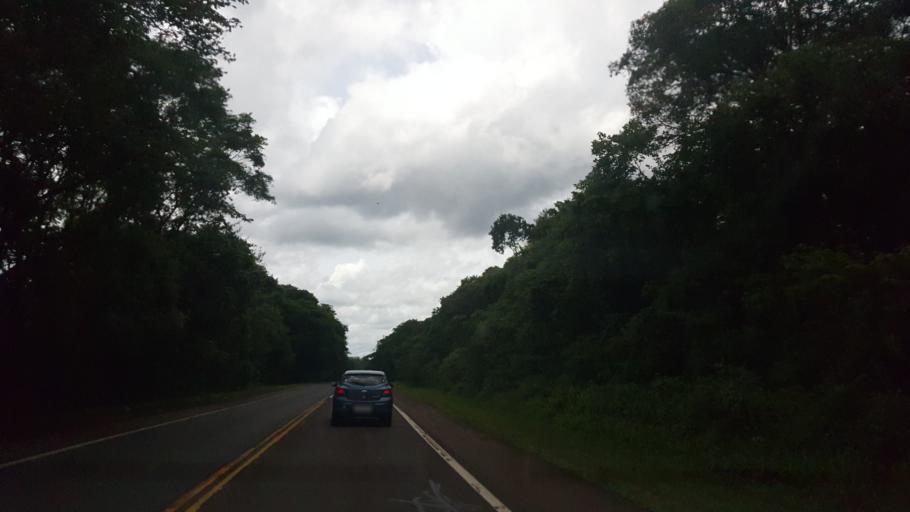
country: AR
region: Misiones
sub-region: Departamento de Iguazu
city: Puerto Iguazu
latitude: -25.6897
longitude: -54.5140
